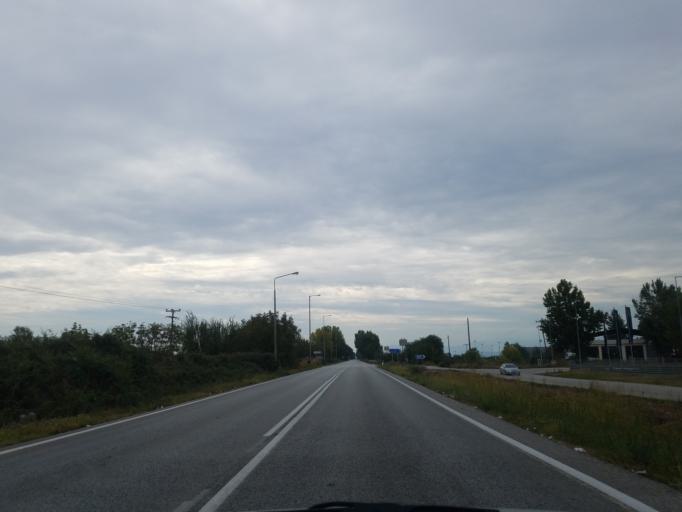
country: GR
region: Thessaly
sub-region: Nomos Kardhitsas
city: Agnantero
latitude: 39.4723
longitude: 21.8483
